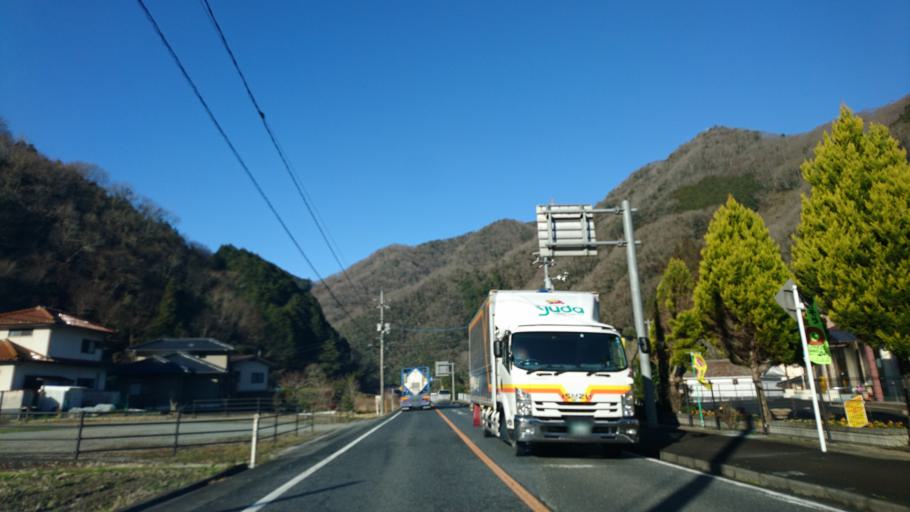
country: JP
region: Okayama
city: Takahashi
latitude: 34.8298
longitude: 133.6300
